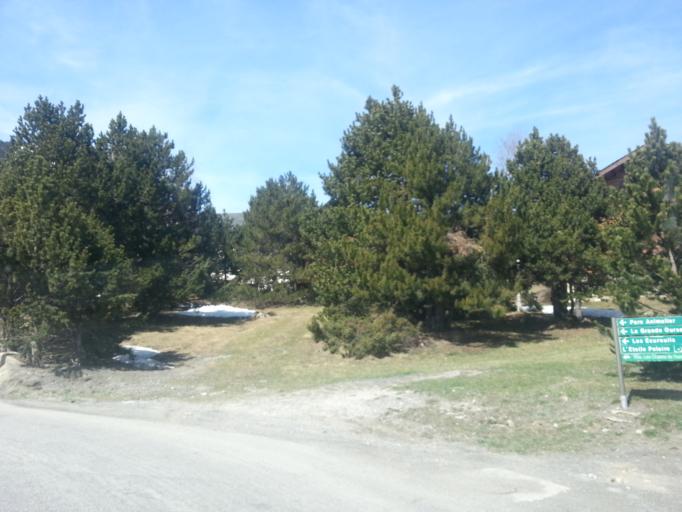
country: ES
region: Catalonia
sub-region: Provincia de Girona
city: Llivia
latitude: 42.5691
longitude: 2.0719
